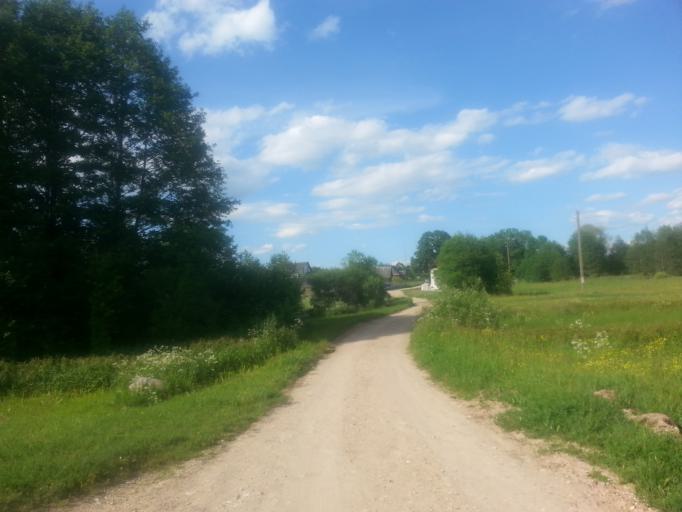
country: BY
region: Minsk
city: Narach
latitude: 54.9748
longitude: 26.6123
